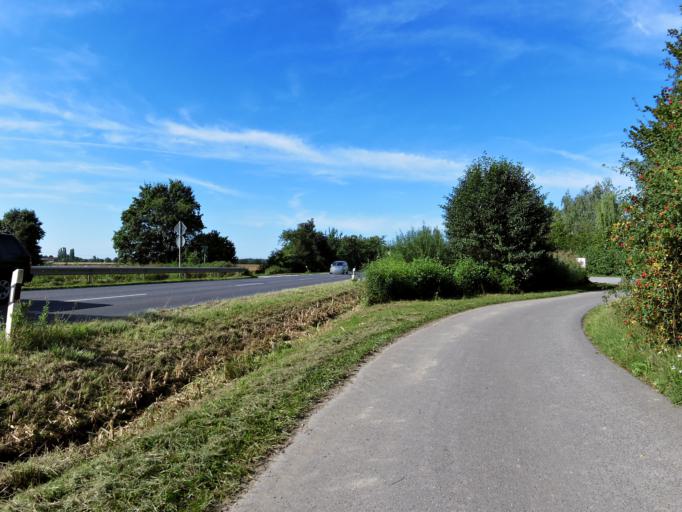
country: DE
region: North Rhine-Westphalia
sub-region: Regierungsbezirk Koln
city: Eschweiler
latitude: 50.8406
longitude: 6.2598
